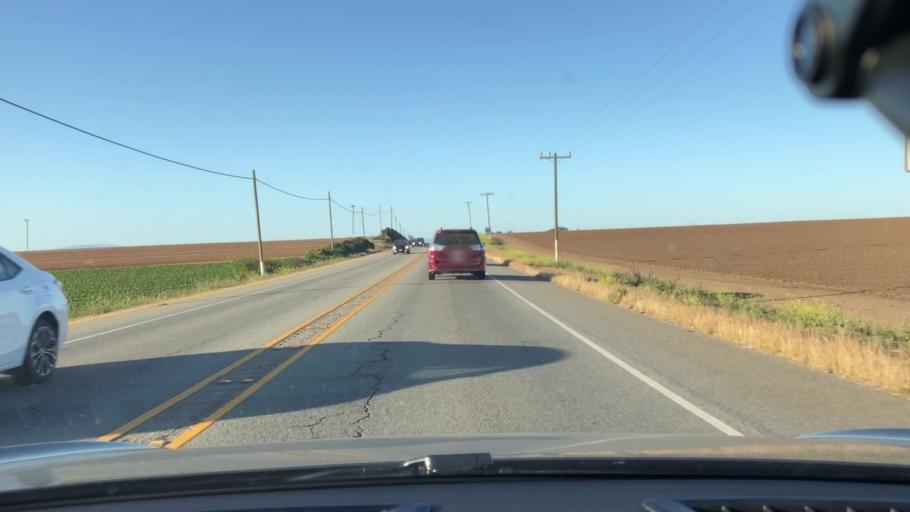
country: US
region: California
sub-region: Monterey County
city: Elkhorn
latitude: 36.8478
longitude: -121.7712
